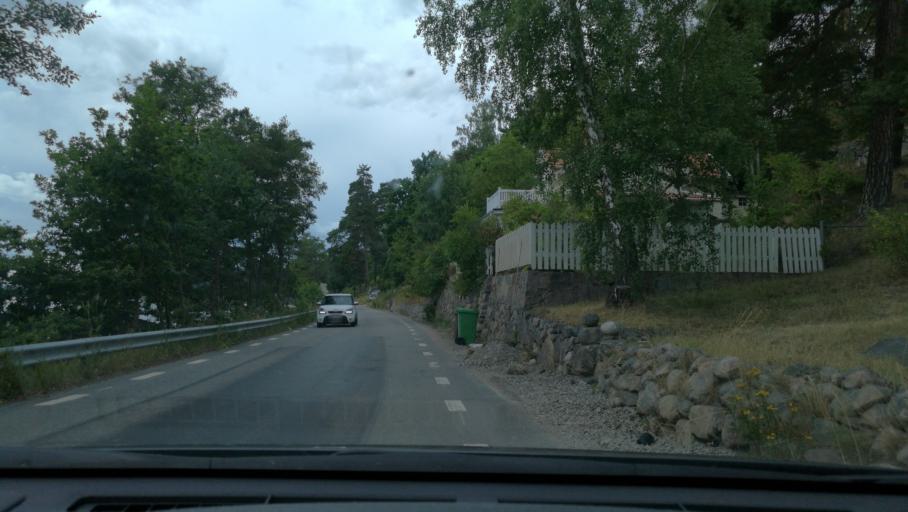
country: SE
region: OEstergoetland
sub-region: Norrkopings Kommun
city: Krokek
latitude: 58.6641
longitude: 16.3625
